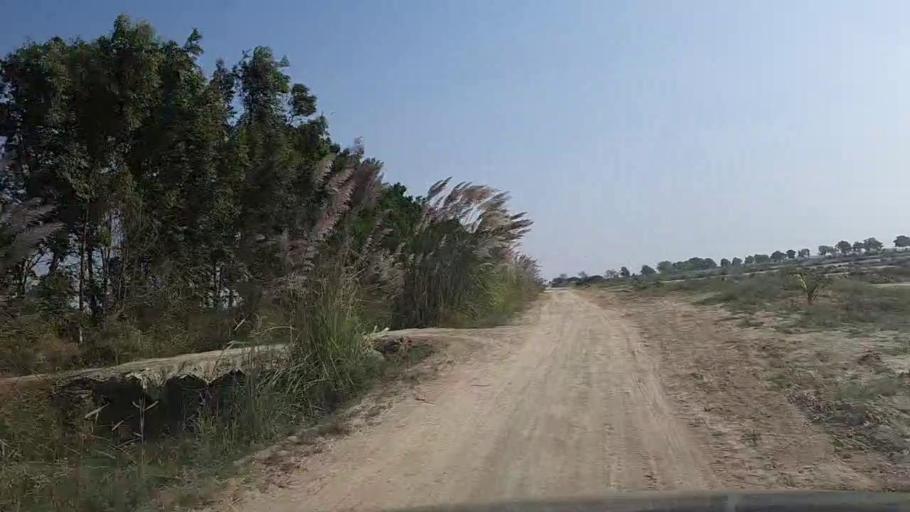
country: PK
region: Sindh
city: Gharo
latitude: 24.7167
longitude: 67.5682
